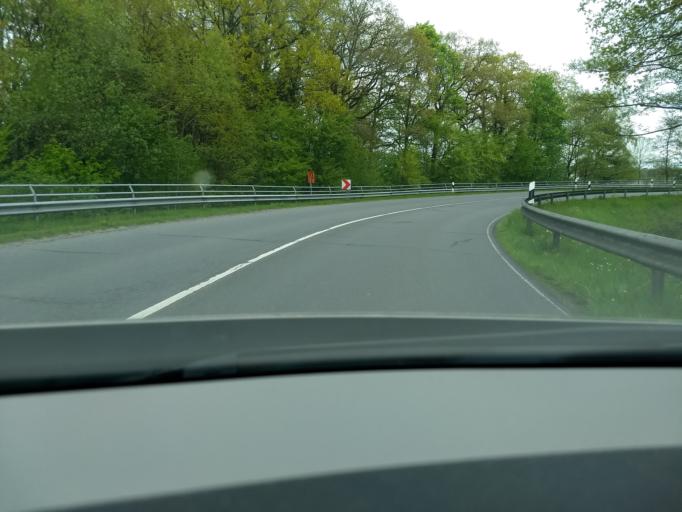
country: DE
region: Lower Saxony
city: Rastede
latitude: 53.2220
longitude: 8.2386
